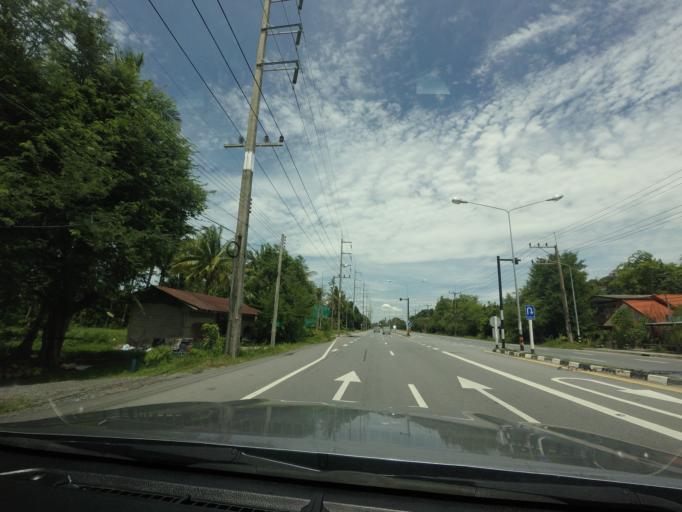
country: TH
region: Songkhla
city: Krasae Sin
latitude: 7.5841
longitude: 100.4063
